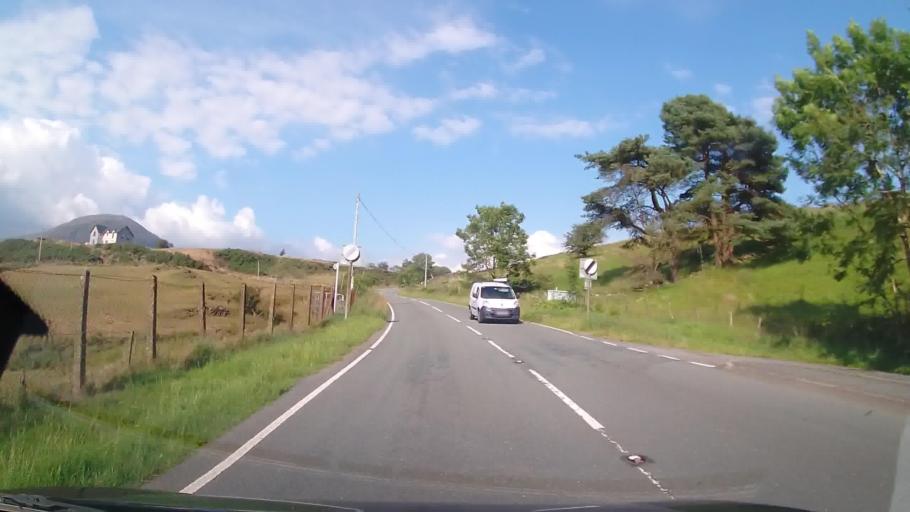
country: GB
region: Wales
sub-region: Gwynedd
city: Ffestiniog
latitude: 52.9608
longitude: -3.9221
